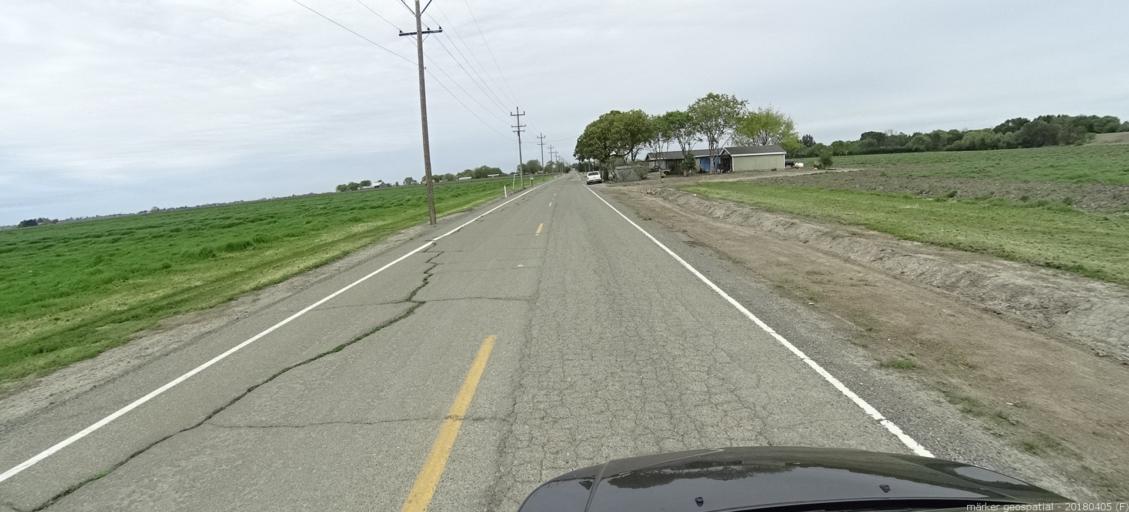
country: US
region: California
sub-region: Sacramento County
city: Walnut Grove
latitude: 38.3005
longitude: -121.5173
